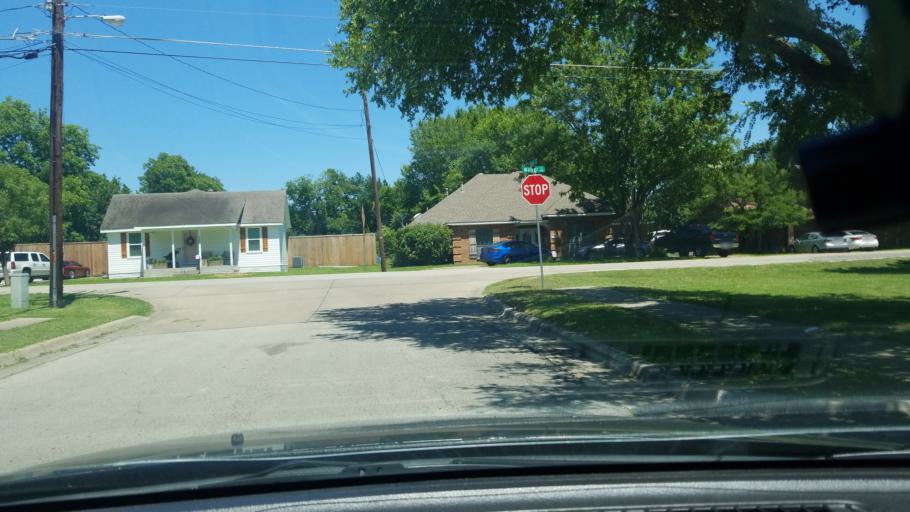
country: US
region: Texas
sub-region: Dallas County
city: Mesquite
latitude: 32.7606
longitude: -96.6055
